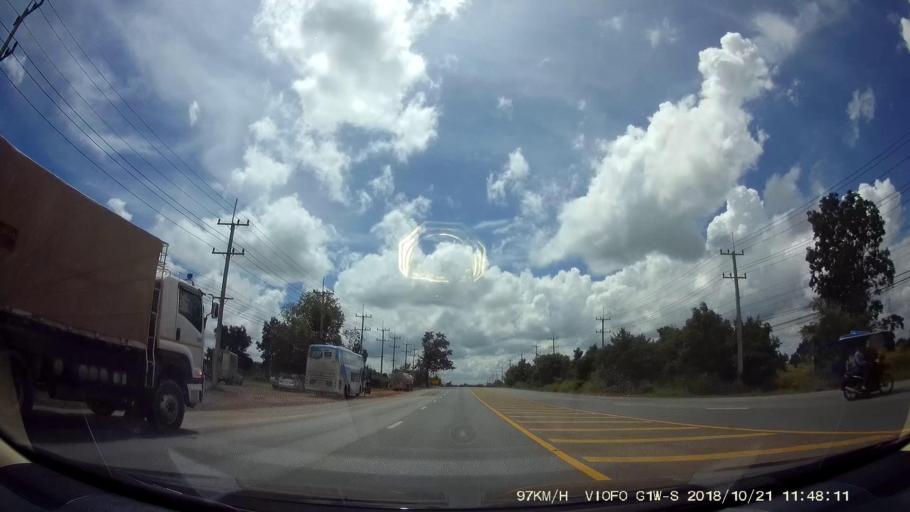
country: TH
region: Chaiyaphum
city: Noen Sa-nga
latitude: 15.6509
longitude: 101.9508
